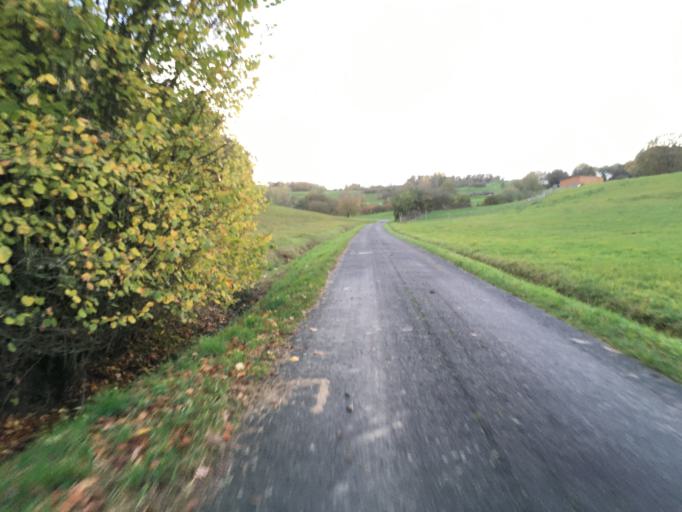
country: DE
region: Baden-Wuerttemberg
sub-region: Karlsruhe Region
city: Rosenberg
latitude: 49.3956
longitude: 9.4836
